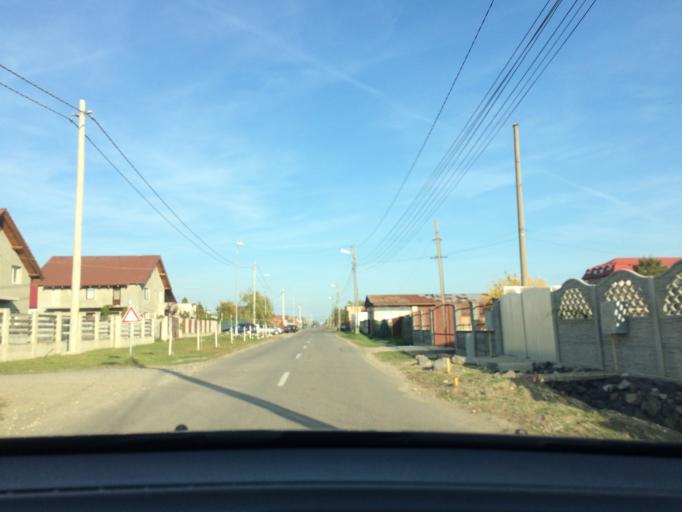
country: RO
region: Timis
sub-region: Oras Recas
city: Recas
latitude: 45.8056
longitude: 21.5095
